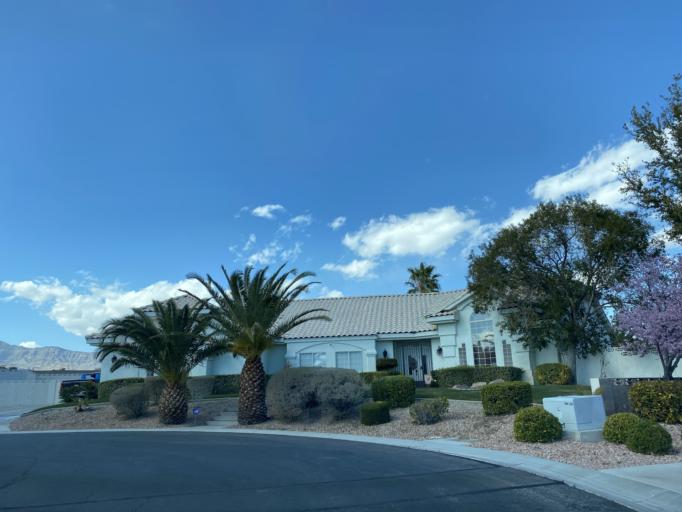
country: US
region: Nevada
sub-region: Clark County
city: Summerlin South
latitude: 36.2742
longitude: -115.2894
